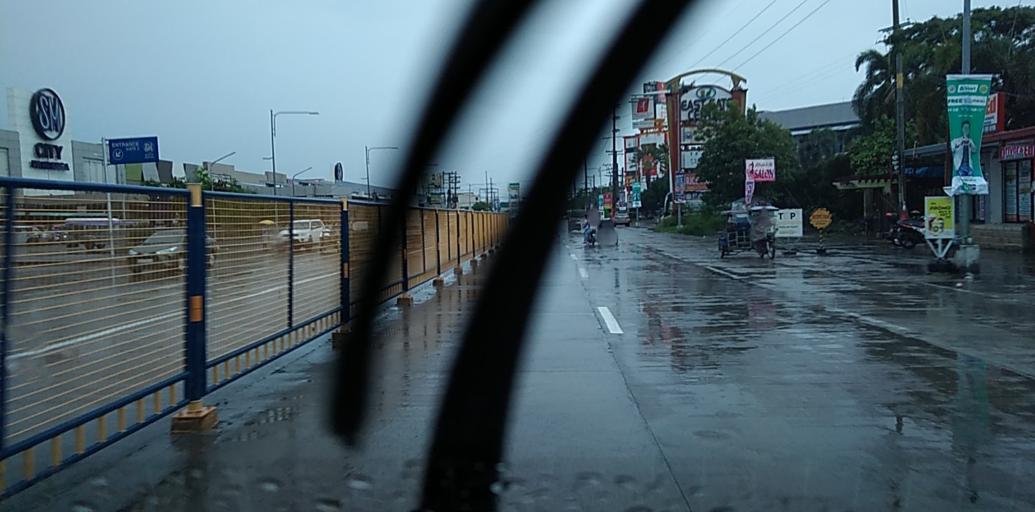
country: PH
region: Central Luzon
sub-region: Province of Pampanga
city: Del Pilar
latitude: 15.0513
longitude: 120.6995
